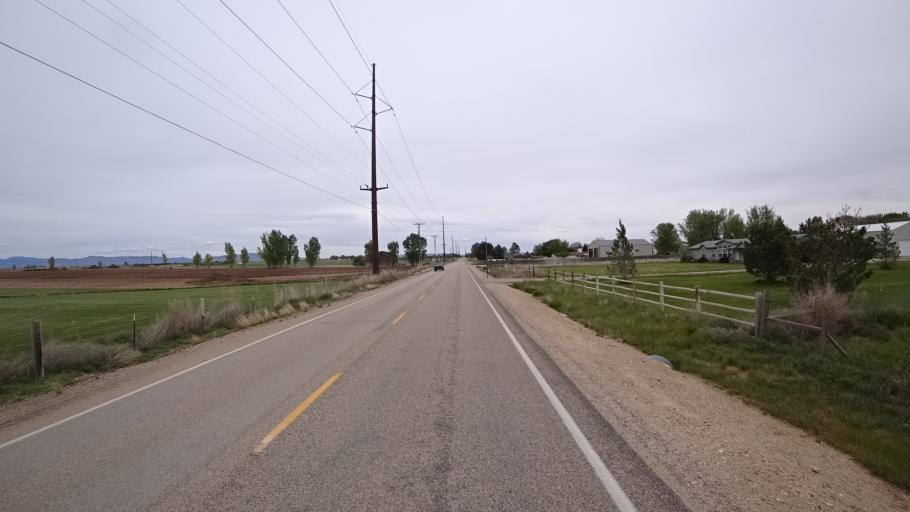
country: US
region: Idaho
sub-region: Ada County
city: Kuna
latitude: 43.4885
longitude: -116.3169
